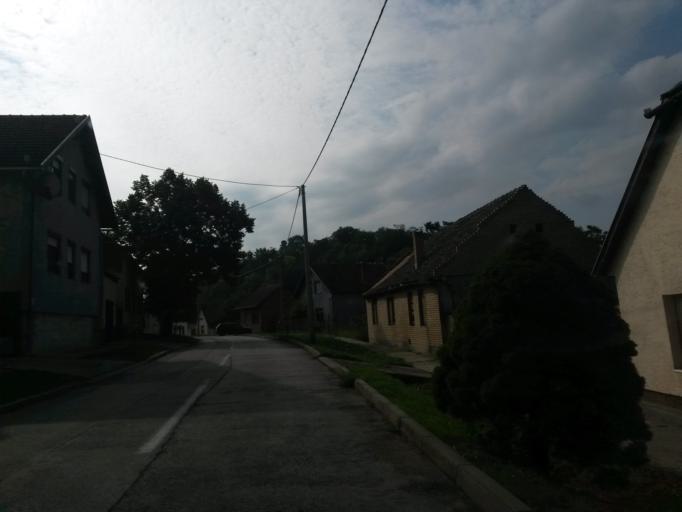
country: HR
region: Vukovarsko-Srijemska
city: Ilok
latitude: 45.2179
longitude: 19.3814
